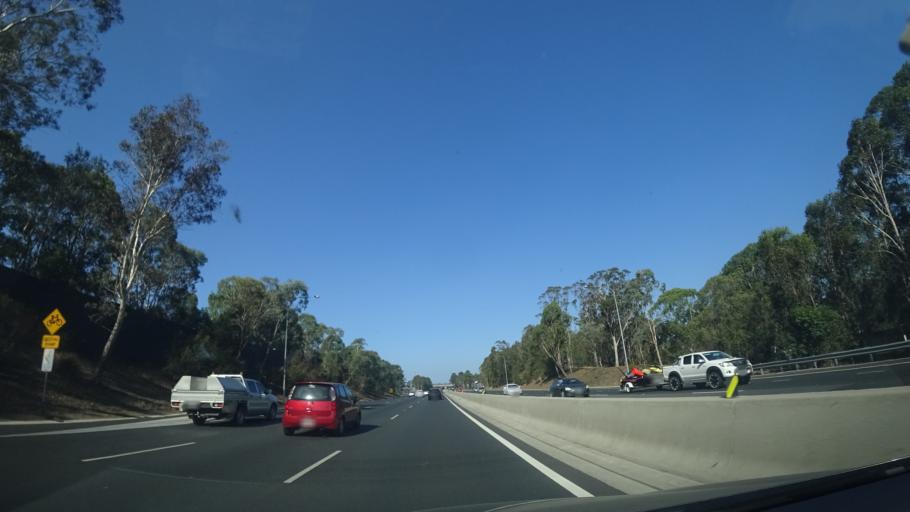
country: AU
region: New South Wales
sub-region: Bankstown
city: Milperra
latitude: -33.9454
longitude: 150.9768
